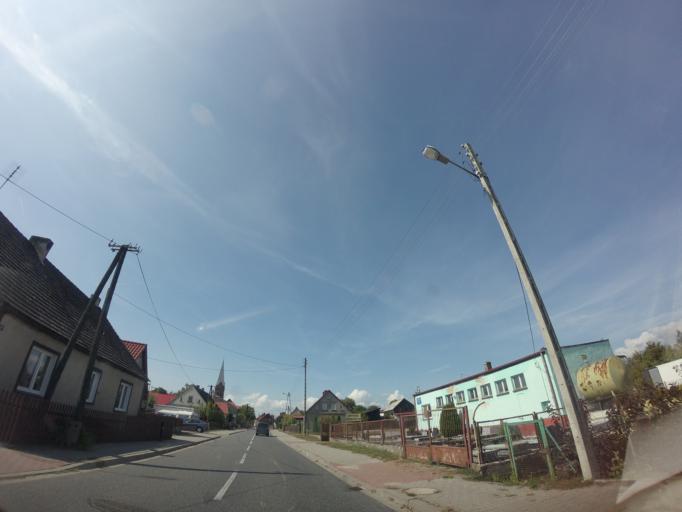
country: PL
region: Lubusz
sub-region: Powiat strzelecko-drezdenecki
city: Stare Kurowo
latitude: 52.7676
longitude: 15.7105
